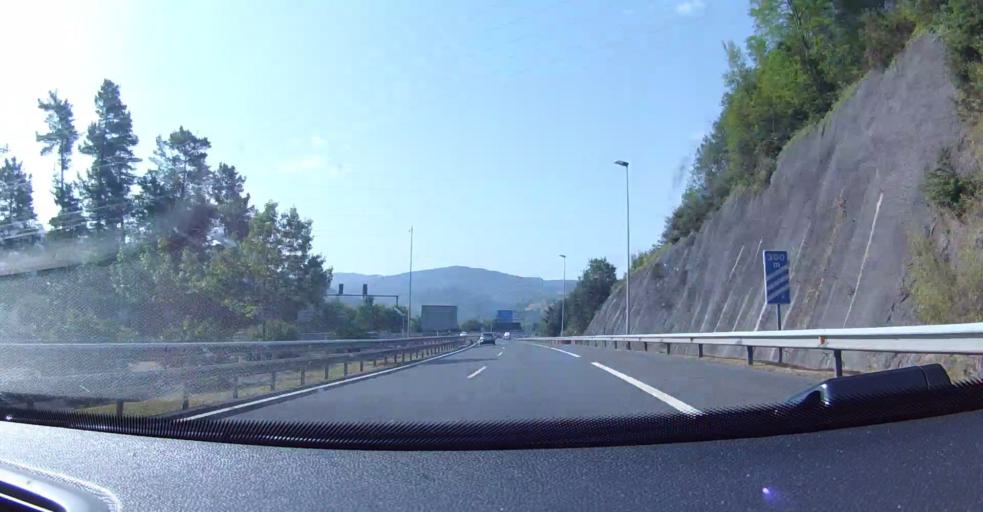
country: ES
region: Basque Country
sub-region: Provincia de Guipuzcoa
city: Bergara
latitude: 43.1340
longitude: -2.4257
